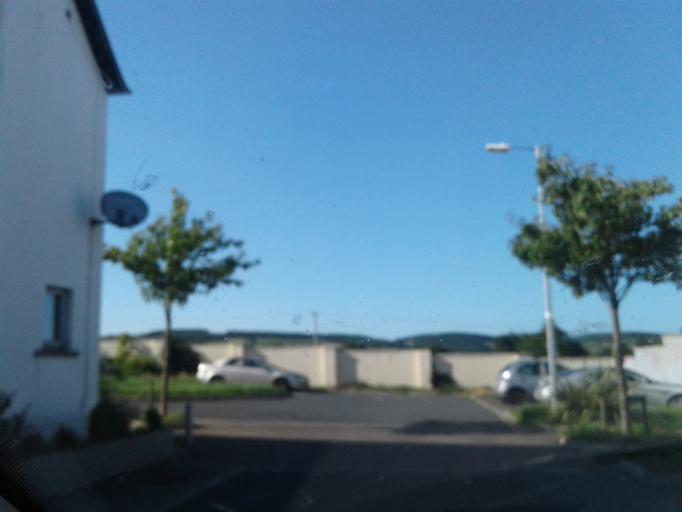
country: IE
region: Leinster
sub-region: Wicklow
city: Enniskerry
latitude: 53.1937
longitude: -6.1862
